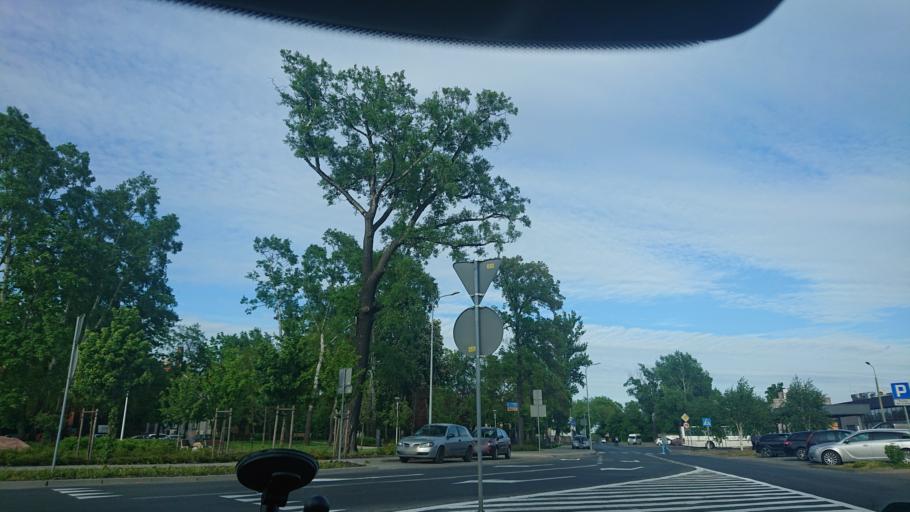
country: PL
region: Greater Poland Voivodeship
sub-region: Powiat gnieznienski
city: Gniezno
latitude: 52.5303
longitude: 17.6023
